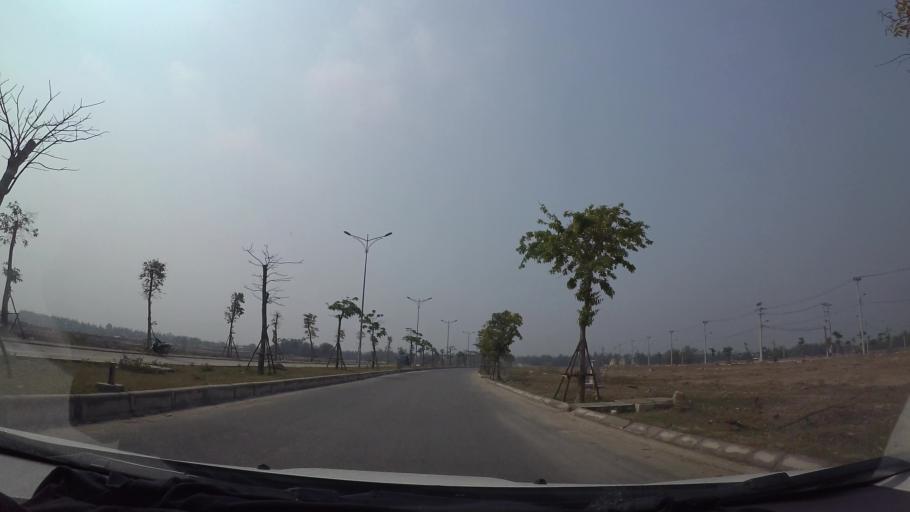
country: VN
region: Da Nang
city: Ngu Hanh Son
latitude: 15.9980
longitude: 108.2478
